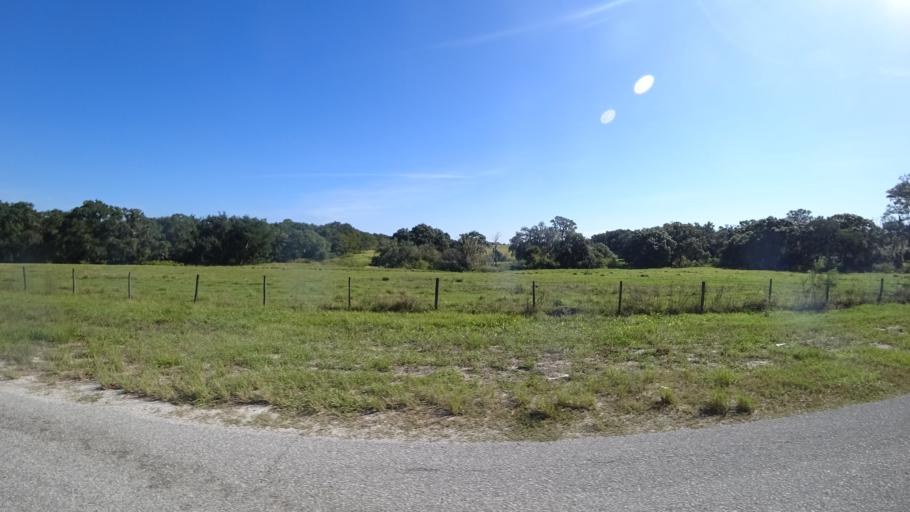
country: US
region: Florida
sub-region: Hillsborough County
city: Wimauma
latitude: 27.6468
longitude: -82.2935
